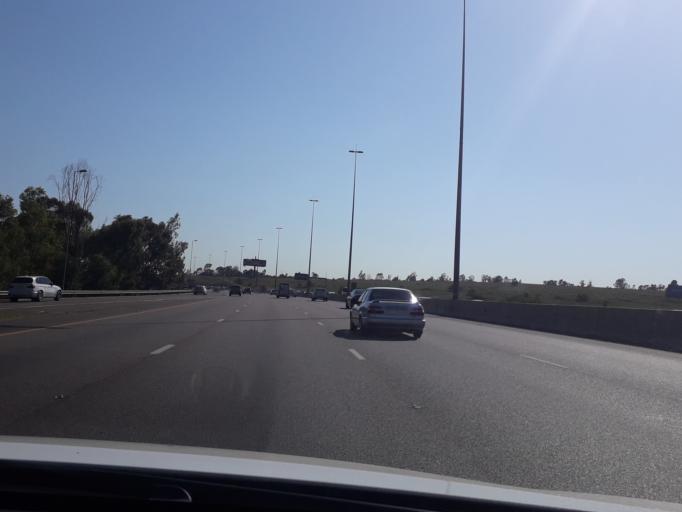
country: ZA
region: Gauteng
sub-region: City of Tshwane Metropolitan Municipality
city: Centurion
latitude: -25.8582
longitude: 28.2213
